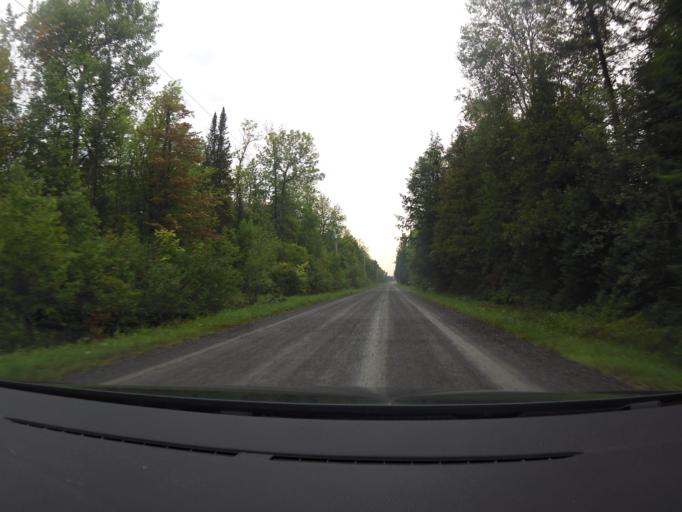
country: CA
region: Ontario
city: Carleton Place
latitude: 45.2086
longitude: -76.1064
